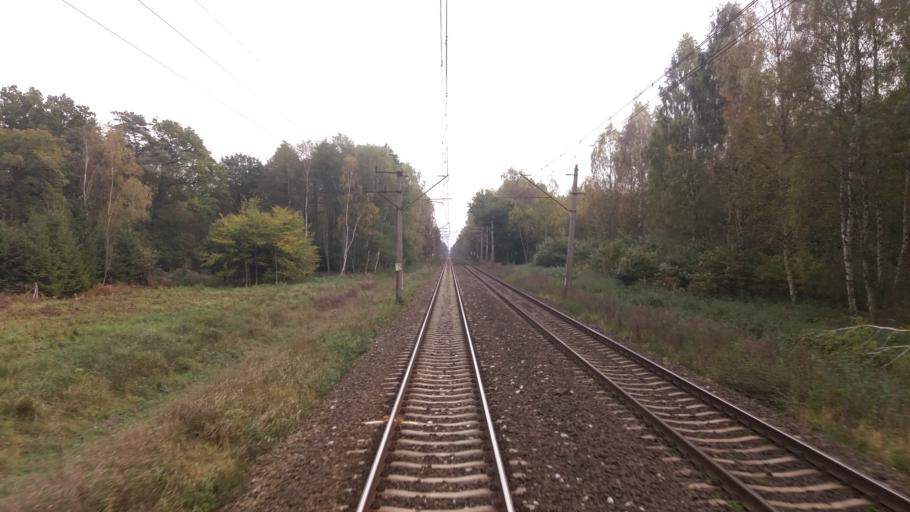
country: PL
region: West Pomeranian Voivodeship
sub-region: Powiat stargardzki
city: Kobylanka
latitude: 53.3782
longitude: 14.8101
